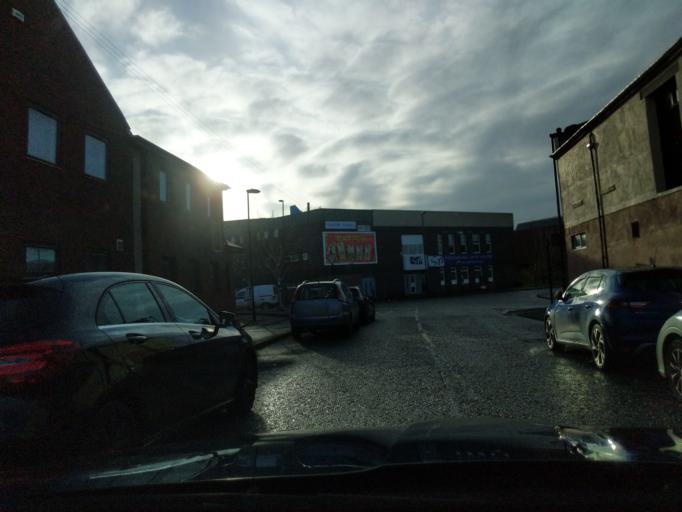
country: GB
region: England
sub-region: Gateshead
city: Felling
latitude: 54.9776
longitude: -1.5757
